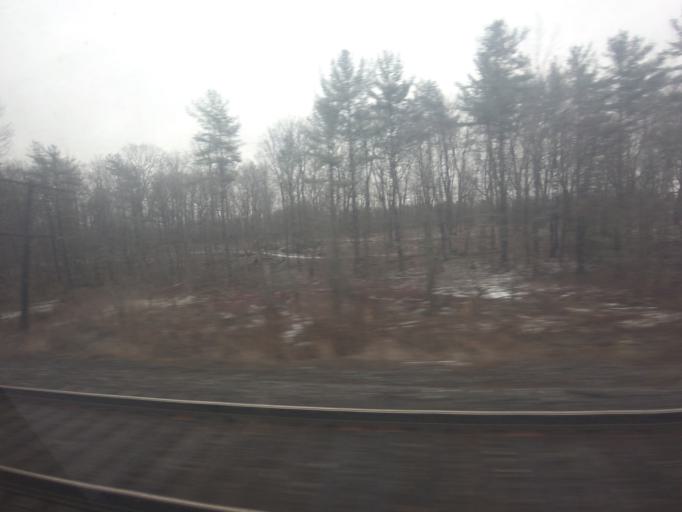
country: CA
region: Ontario
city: Kingston
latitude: 44.2345
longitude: -76.6276
